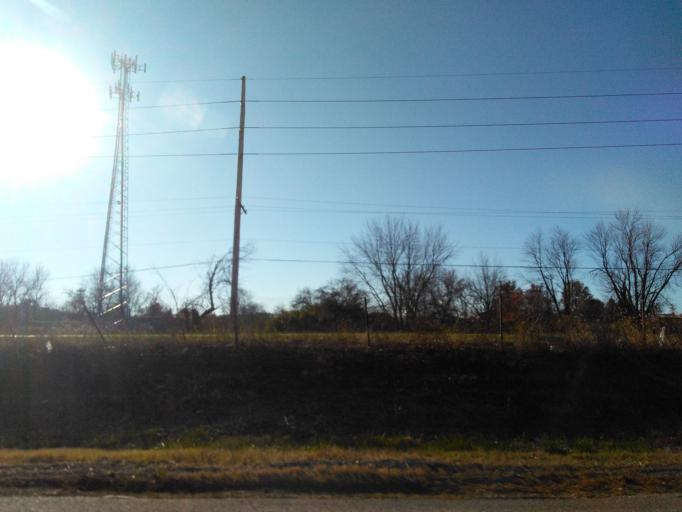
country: US
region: Illinois
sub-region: Madison County
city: Maryville
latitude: 38.7089
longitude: -89.9527
